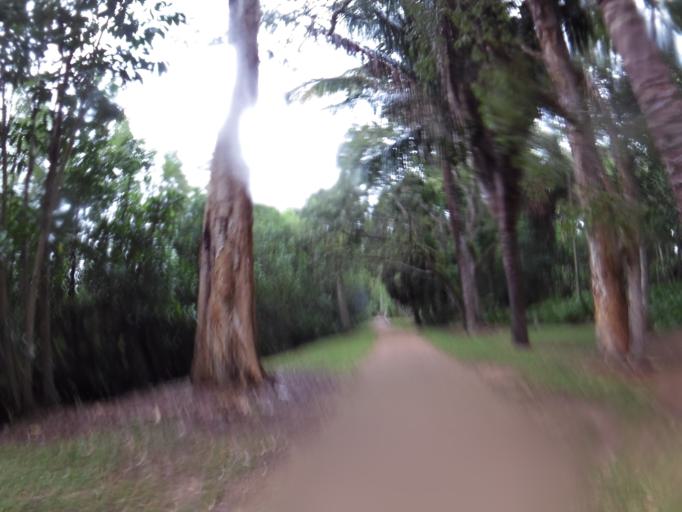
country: AU
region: Queensland
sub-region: Cairns
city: Cairns
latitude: -16.9020
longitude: 145.7507
